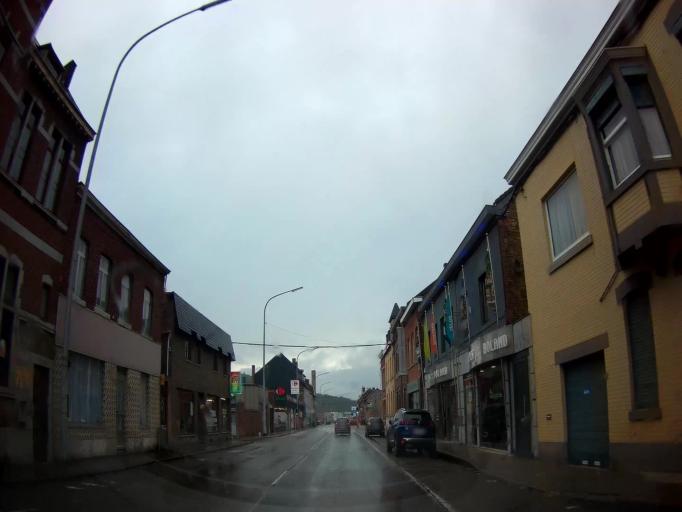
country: BE
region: Wallonia
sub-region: Province de Liege
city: Trooz
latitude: 50.5783
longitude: 5.6743
